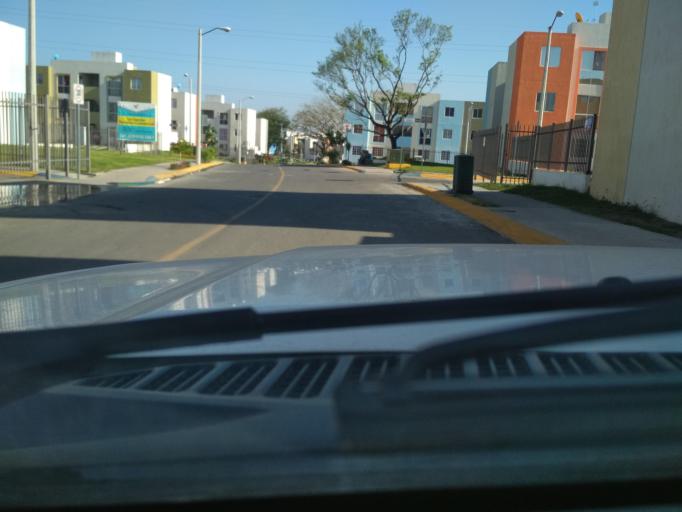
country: MX
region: Veracruz
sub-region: Veracruz
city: Las Amapolas
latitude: 19.1465
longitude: -96.2351
